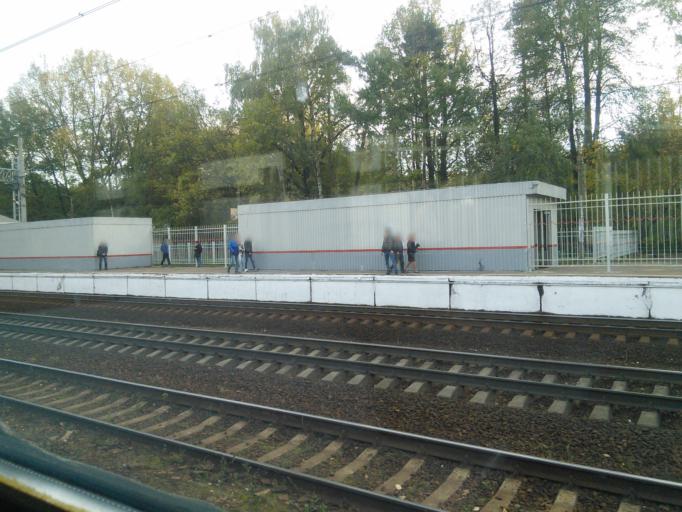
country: RU
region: Moskovskaya
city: Levoberezhnaya
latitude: 55.8874
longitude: 37.4681
